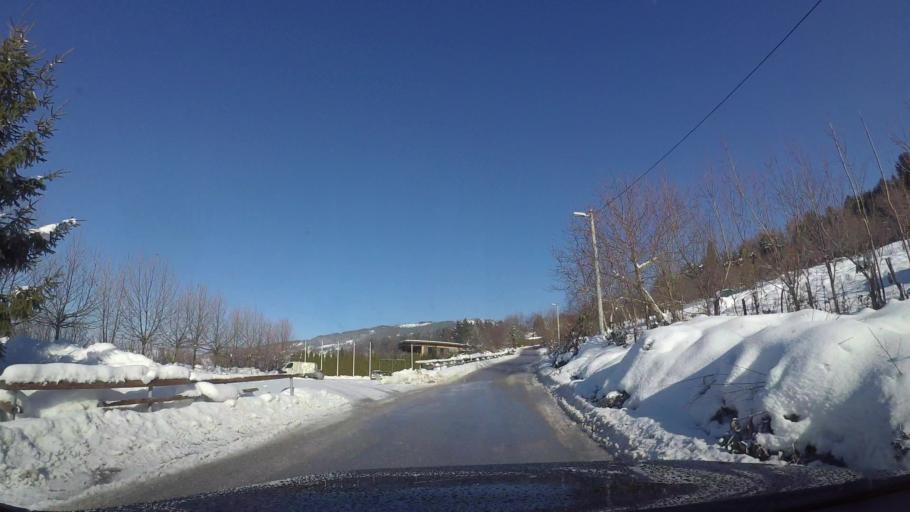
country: BA
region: Federation of Bosnia and Herzegovina
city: Kobilja Glava
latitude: 43.8844
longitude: 18.4098
